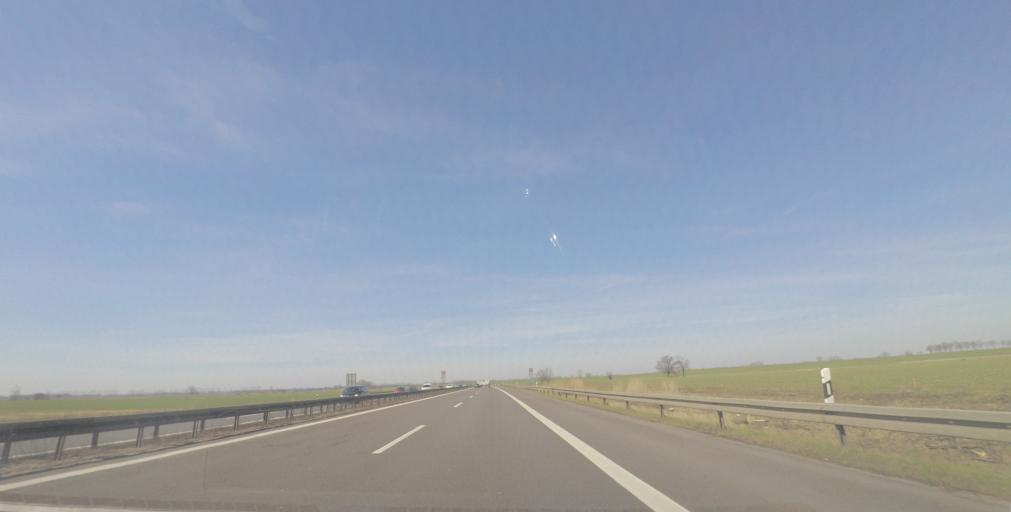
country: DE
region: Brandenburg
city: Kremmen
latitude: 52.7382
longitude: 12.9147
